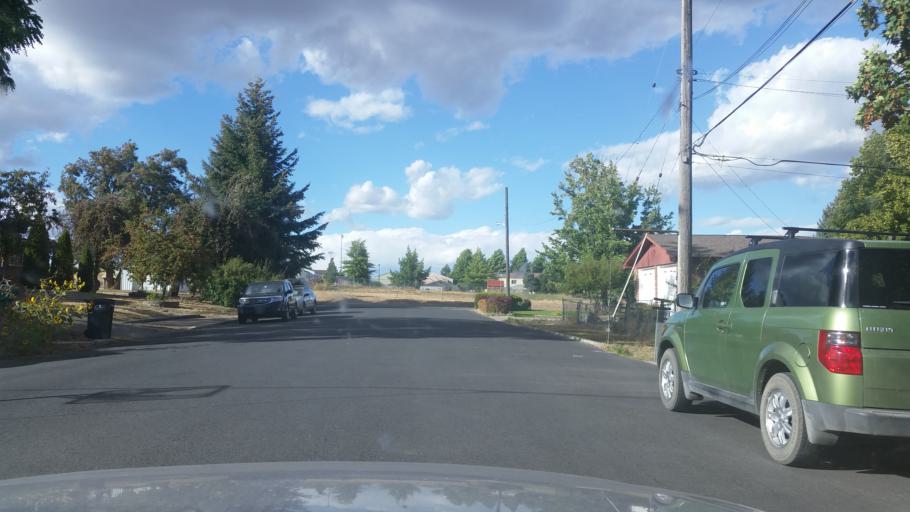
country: US
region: Washington
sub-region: Spokane County
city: Cheney
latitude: 47.4845
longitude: -117.5898
